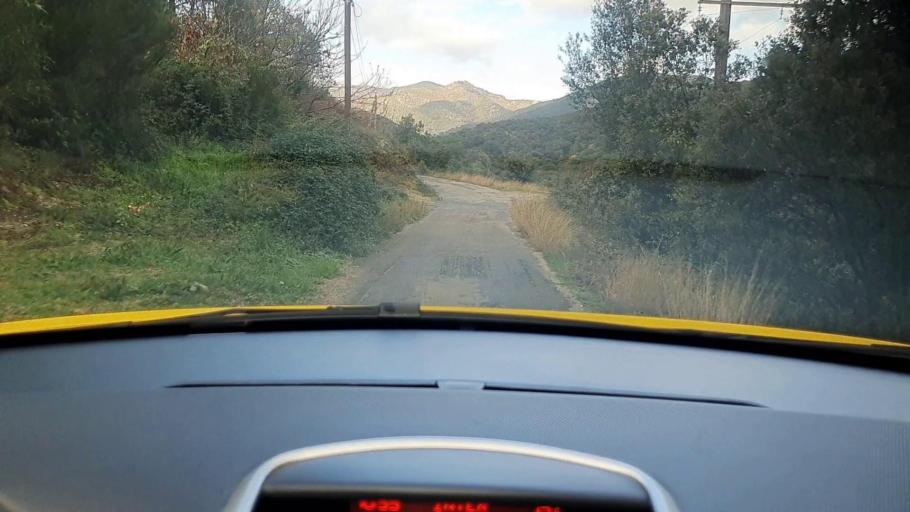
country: FR
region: Languedoc-Roussillon
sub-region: Departement du Gard
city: Lasalle
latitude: 44.0536
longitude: 3.8272
